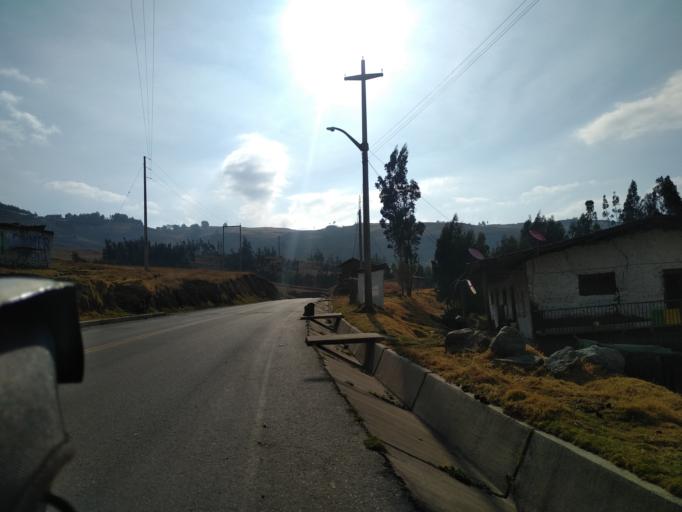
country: PE
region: La Libertad
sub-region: Provincia de Otuzco
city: Agallpampa
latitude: -7.9957
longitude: -78.5244
